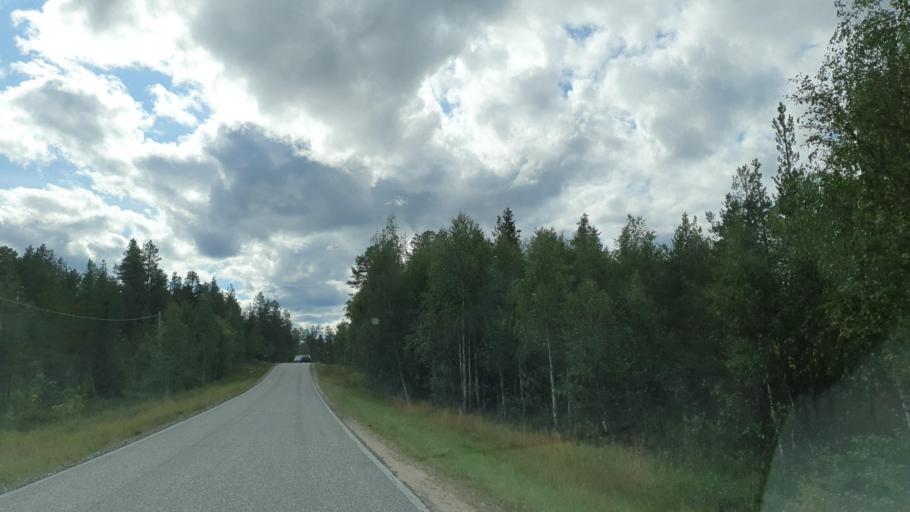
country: FI
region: Lapland
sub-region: Tunturi-Lappi
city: Muonio
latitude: 67.8552
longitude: 24.1000
